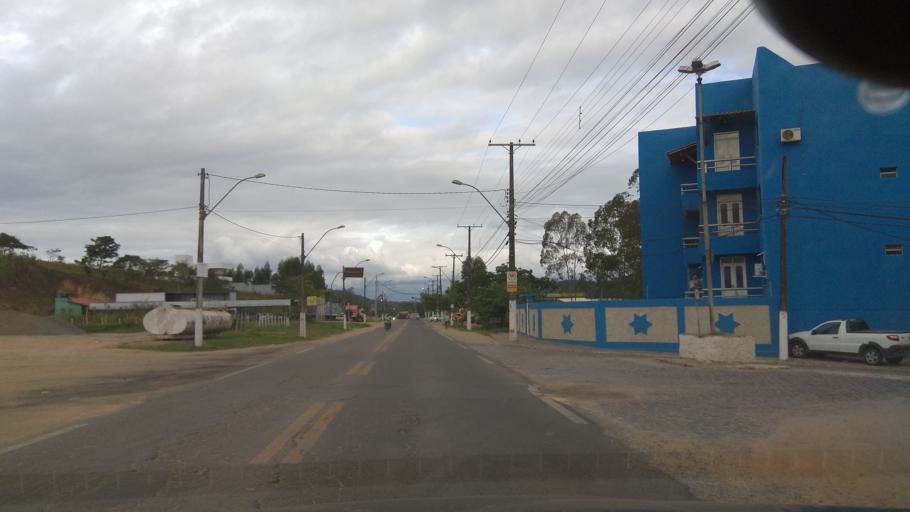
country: BR
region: Bahia
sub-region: Ipiau
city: Ipiau
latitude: -14.1399
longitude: -39.7292
